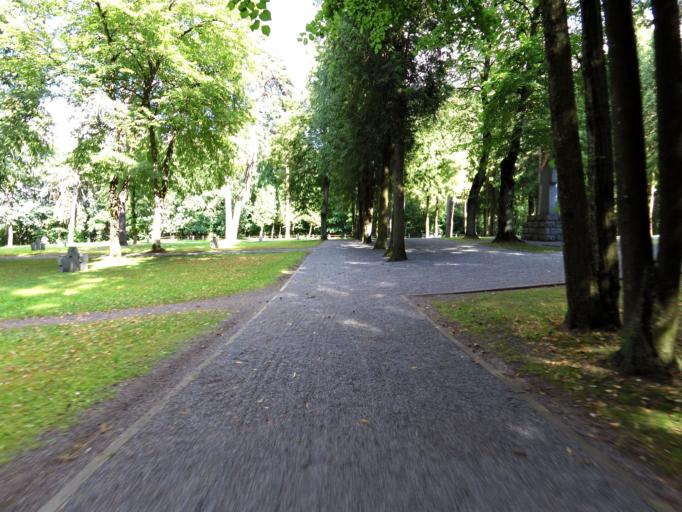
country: LT
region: Vilnius County
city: Vilkpede
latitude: 54.6839
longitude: 25.2479
